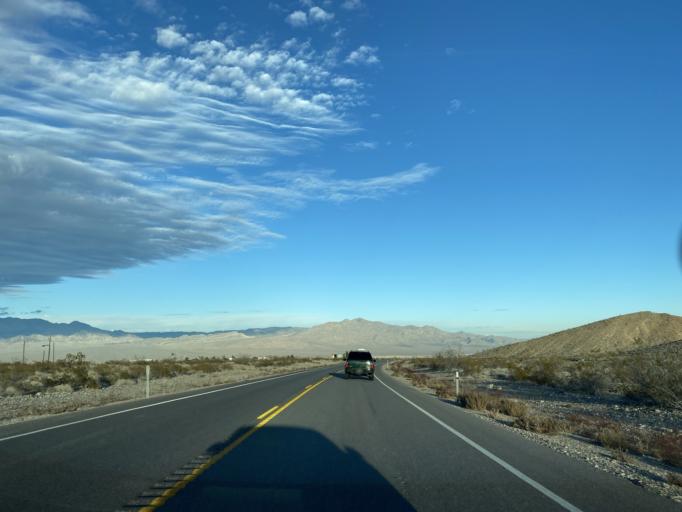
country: US
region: Nevada
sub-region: Clark County
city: Summerlin South
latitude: 36.3055
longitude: -115.4051
